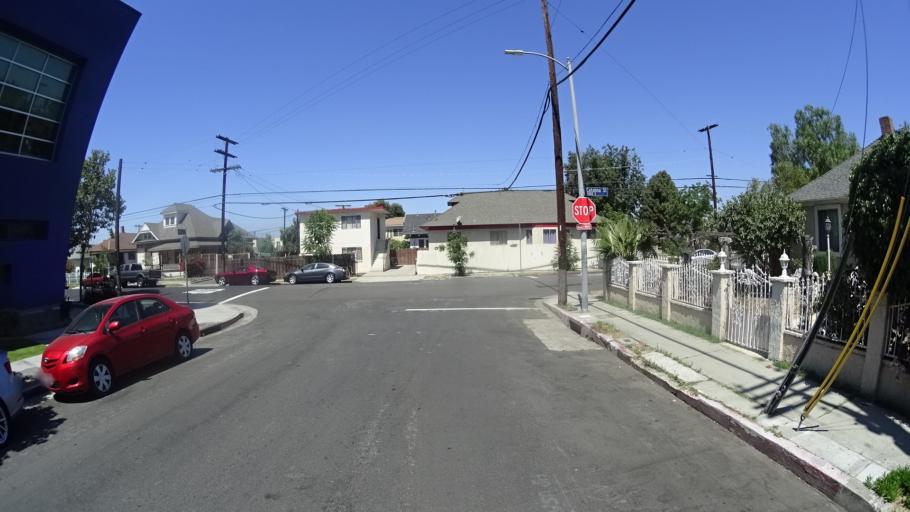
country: US
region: California
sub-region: Los Angeles County
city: Los Angeles
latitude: 34.0270
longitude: -118.2934
